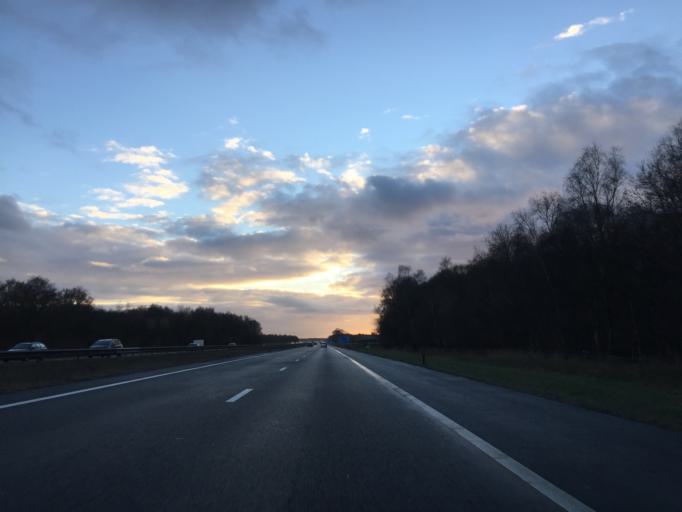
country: NL
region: Friesland
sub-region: Gemeente Smallingerland
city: Boornbergum
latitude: 53.0720
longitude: 6.0618
